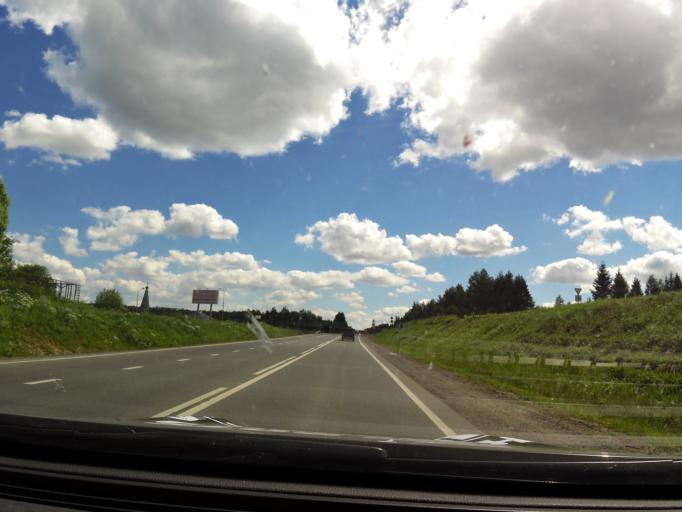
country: RU
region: Vologda
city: Molochnoye
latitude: 59.2787
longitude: 39.7107
